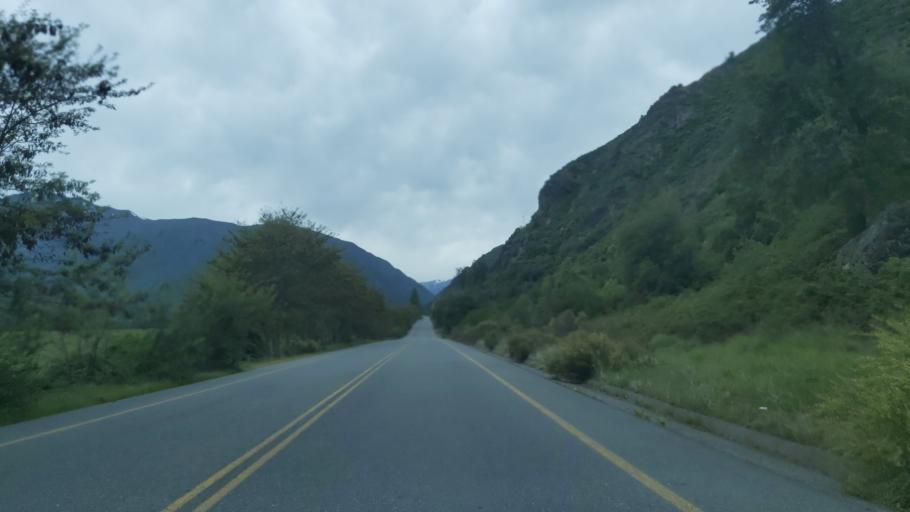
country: CL
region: Maule
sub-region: Provincia de Linares
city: Colbun
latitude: -35.8121
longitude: -70.8671
